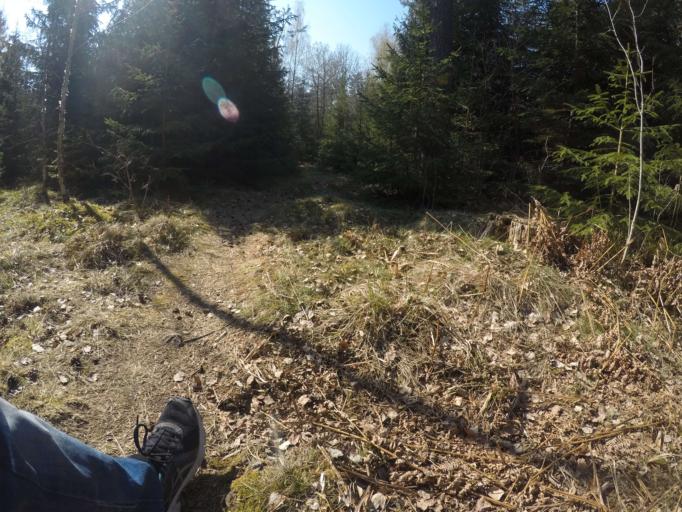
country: SE
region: Vaestmanland
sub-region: Hallstahammars Kommun
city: Kolback
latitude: 59.5350
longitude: 16.2760
